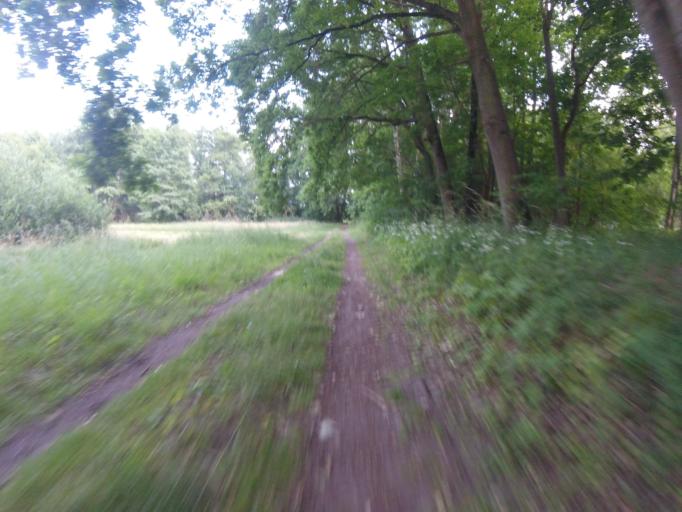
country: DE
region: Brandenburg
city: Bestensee
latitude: 52.2658
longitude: 13.6367
